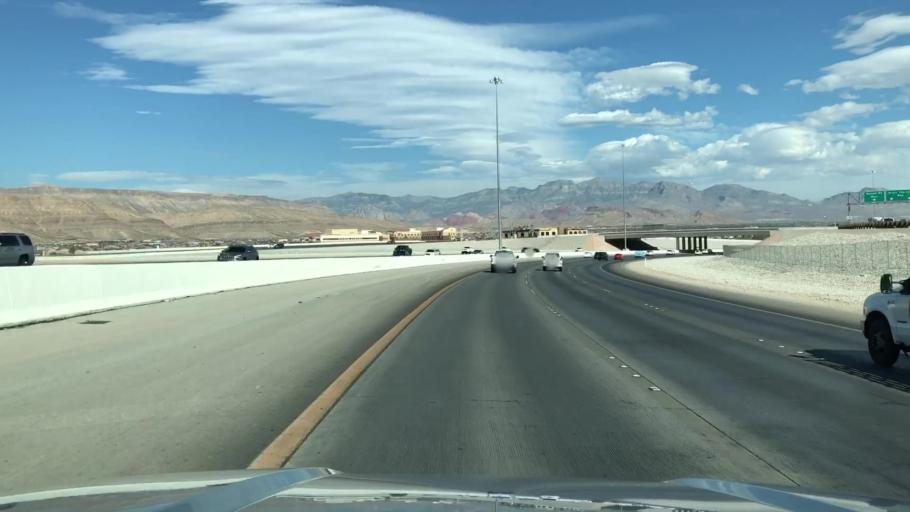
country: US
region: Nevada
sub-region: Clark County
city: Spring Valley
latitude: 36.0676
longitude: -115.2860
